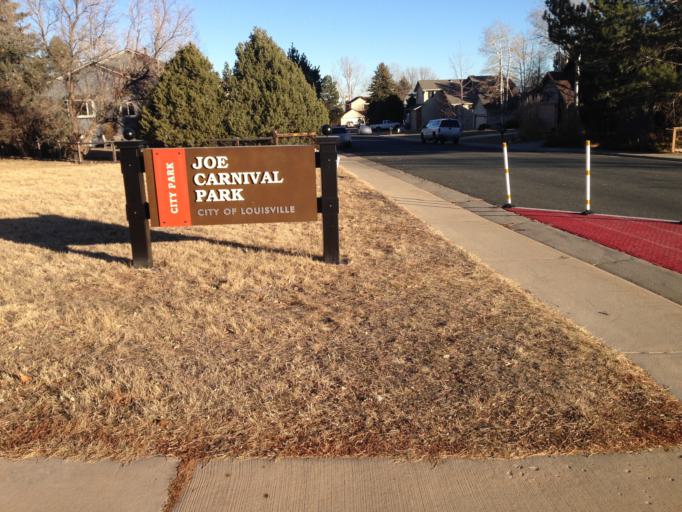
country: US
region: Colorado
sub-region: Boulder County
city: Louisville
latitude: 39.9829
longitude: -105.1620
